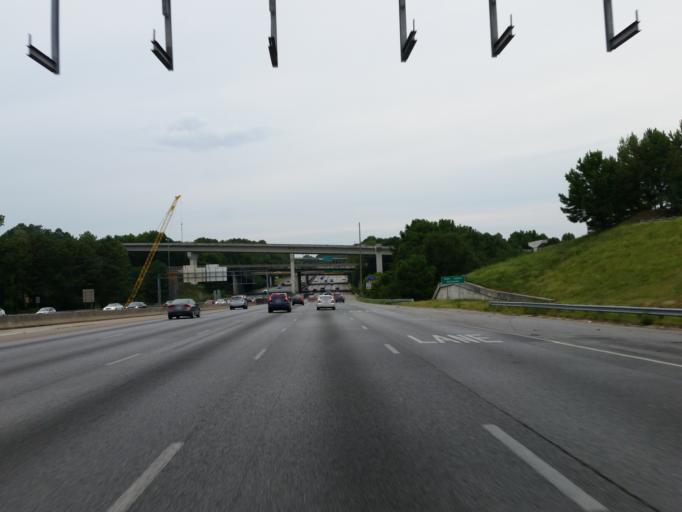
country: US
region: Georgia
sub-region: Cobb County
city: Vinings
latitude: 33.8879
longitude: -84.4588
